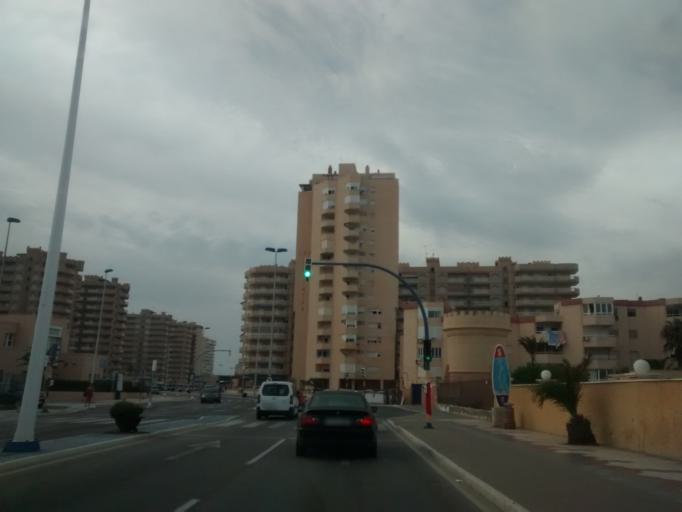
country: ES
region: Murcia
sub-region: Murcia
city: La Manga del Mar Menor
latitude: 37.6762
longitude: -0.7314
